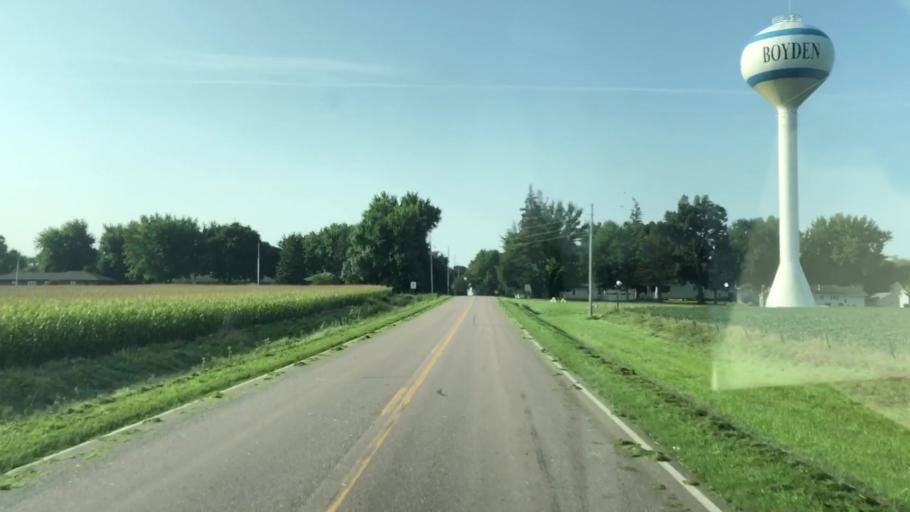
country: US
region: Iowa
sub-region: Sioux County
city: Hull
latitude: 43.1948
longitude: -96.0003
